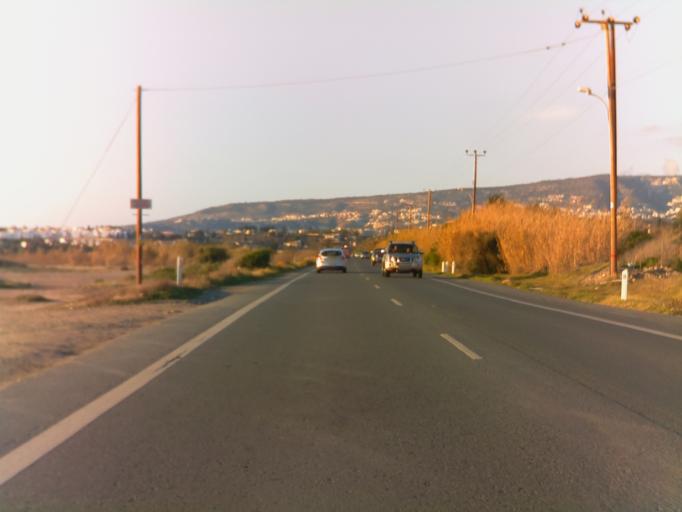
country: CY
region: Pafos
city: Kissonerga
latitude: 34.8406
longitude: 32.3883
